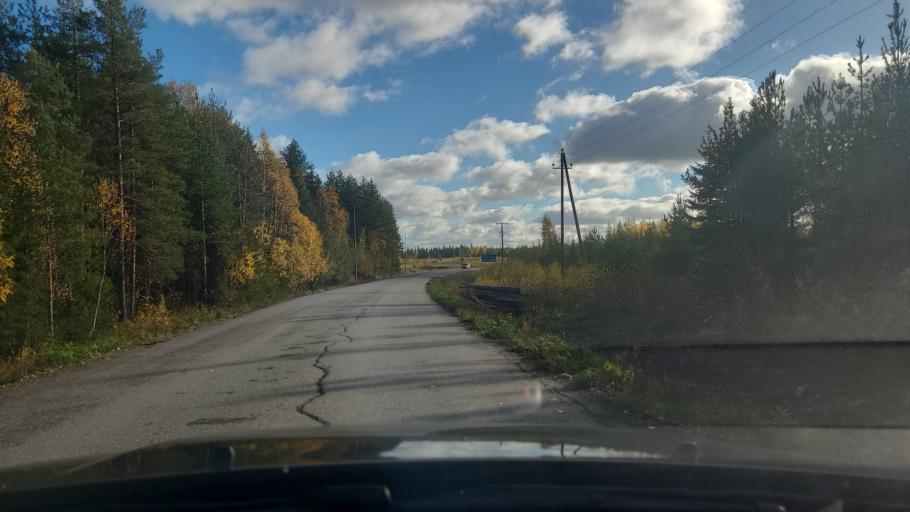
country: FI
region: Southern Savonia
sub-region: Pieksaemaeki
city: Juva
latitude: 61.8037
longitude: 27.5933
